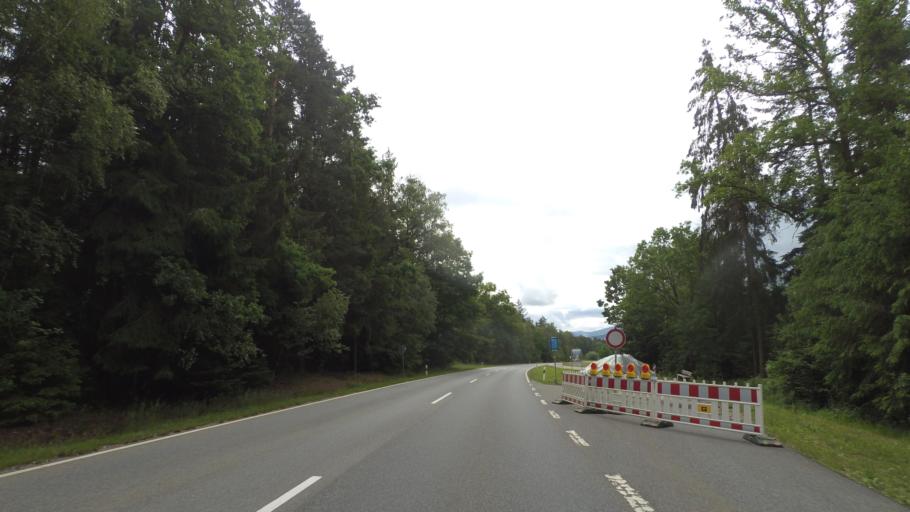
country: DE
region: Bavaria
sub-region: Lower Bavaria
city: Prackenbach
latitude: 49.0872
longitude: 12.8514
